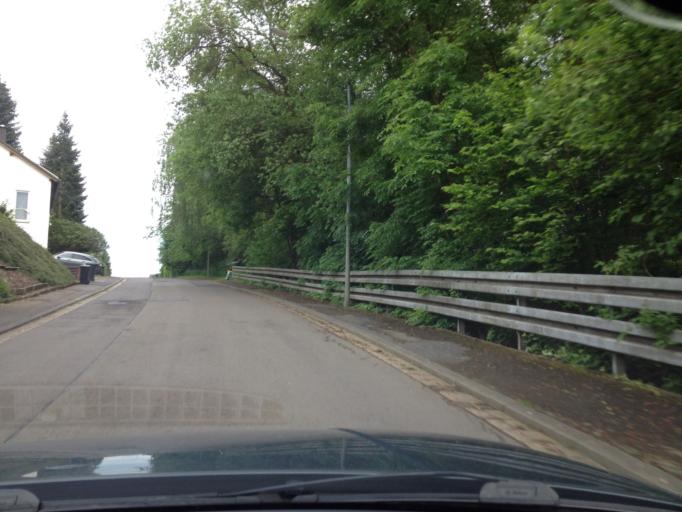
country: DE
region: Saarland
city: Schiffweiler
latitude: 49.3711
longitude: 7.1146
